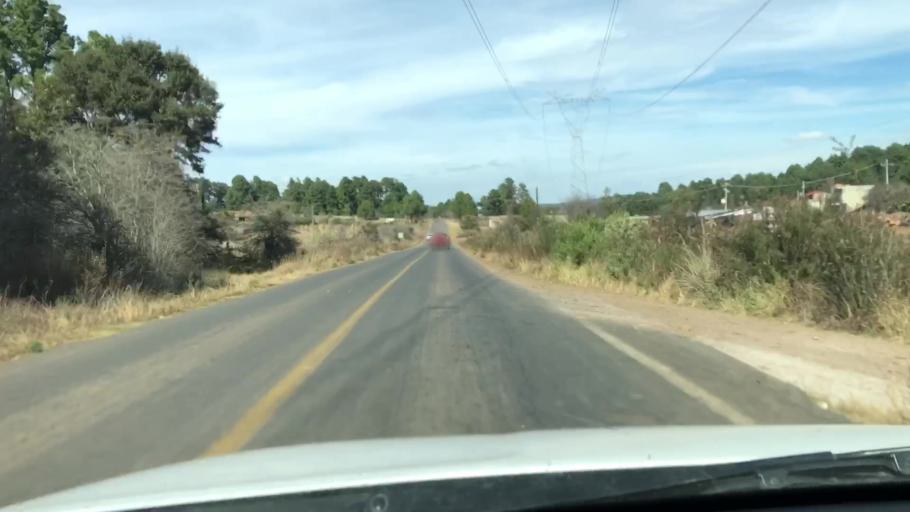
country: MX
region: Jalisco
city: Chiquilistlan
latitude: 20.1073
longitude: -103.7181
